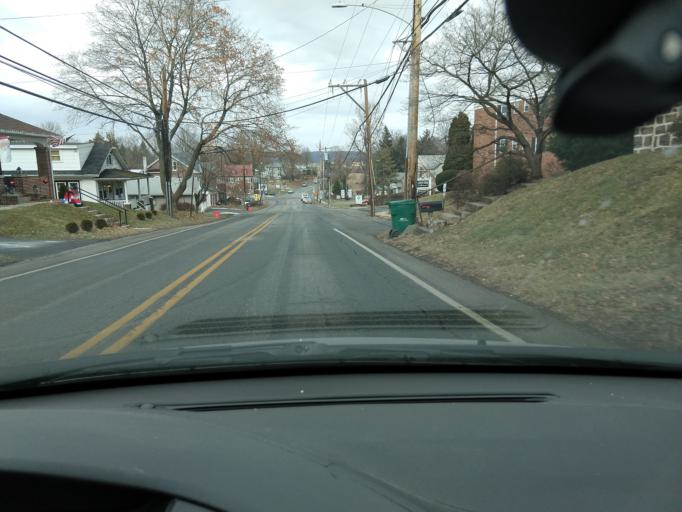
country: US
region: Pennsylvania
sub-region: Chester County
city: South Pottstown
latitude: 40.2319
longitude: -75.6544
